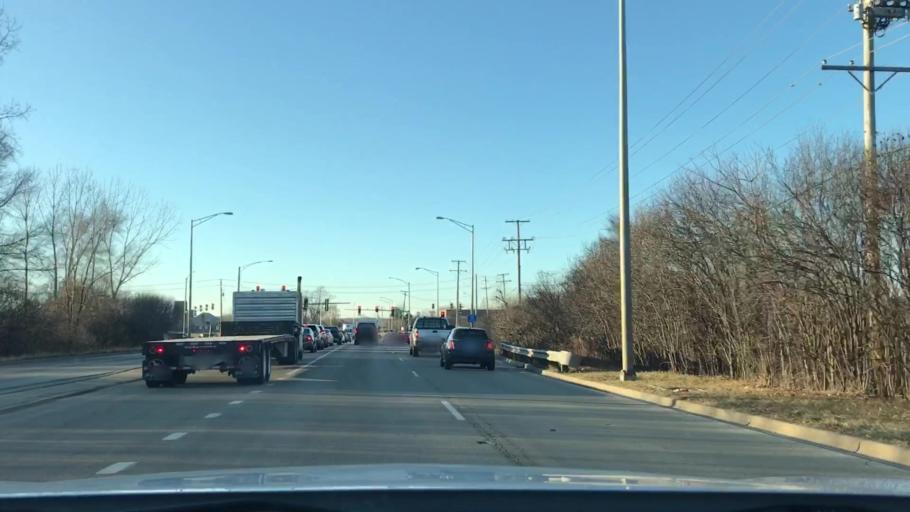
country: US
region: Illinois
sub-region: Kane County
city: Sleepy Hollow
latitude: 42.0642
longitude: -88.3338
